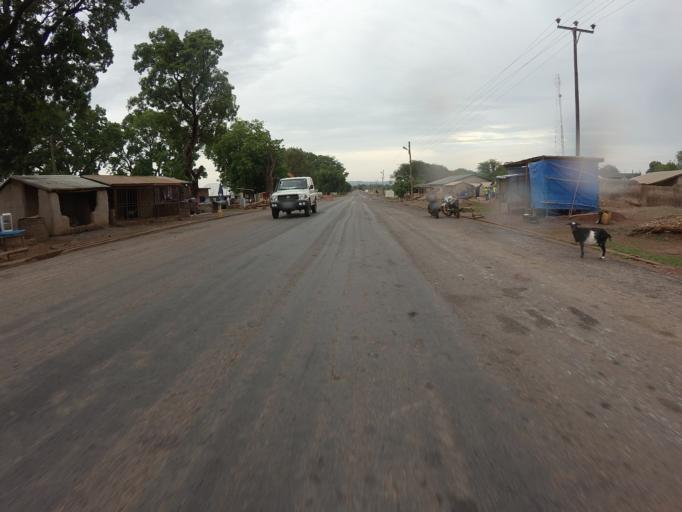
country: GH
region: Upper East
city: Bolgatanga
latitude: 10.8596
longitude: -0.6643
